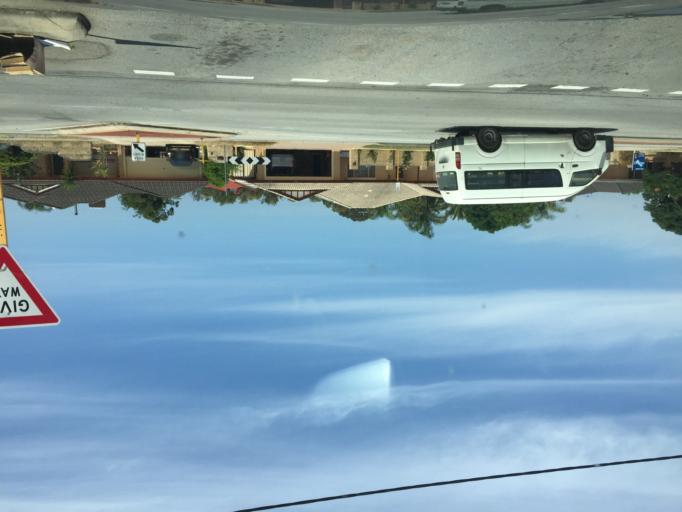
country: AU
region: Western Australia
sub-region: Gosnells
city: Thornlie
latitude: -32.0785
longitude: 115.9575
